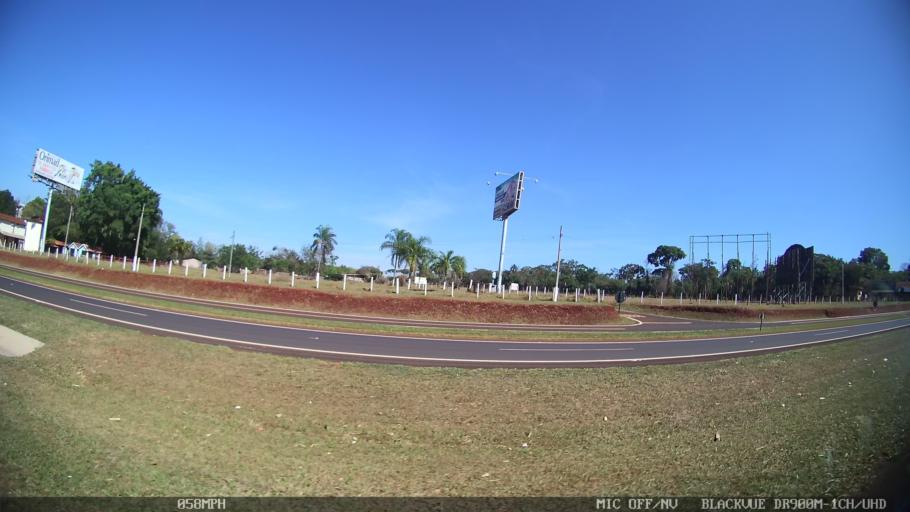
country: BR
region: Sao Paulo
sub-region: Ribeirao Preto
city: Ribeirao Preto
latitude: -21.2149
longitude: -47.8383
